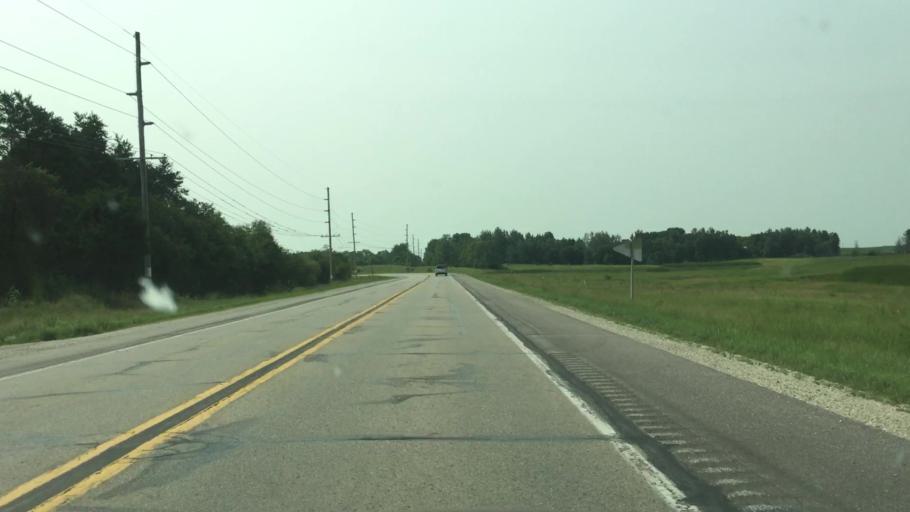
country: US
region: Iowa
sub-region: Dickinson County
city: Milford
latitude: 43.3483
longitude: -95.1798
